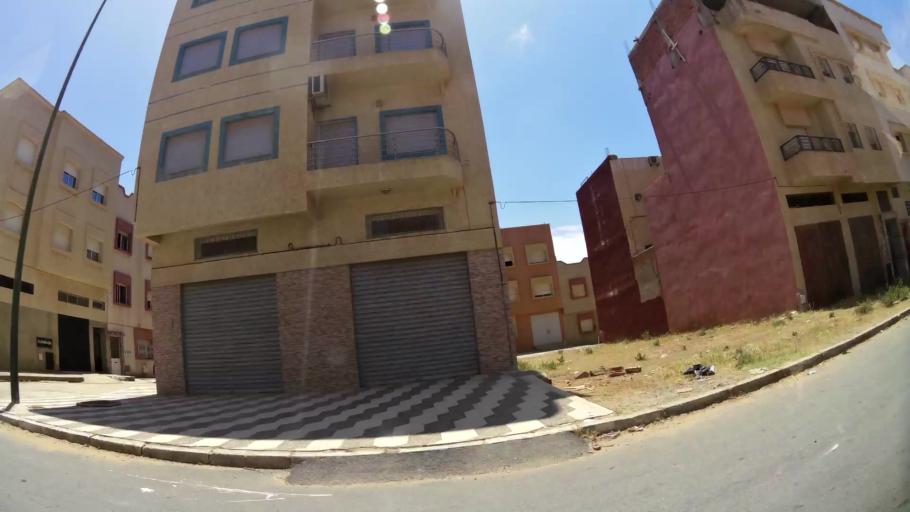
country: MA
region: Gharb-Chrarda-Beni Hssen
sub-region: Kenitra Province
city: Kenitra
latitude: 34.2338
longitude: -6.6053
